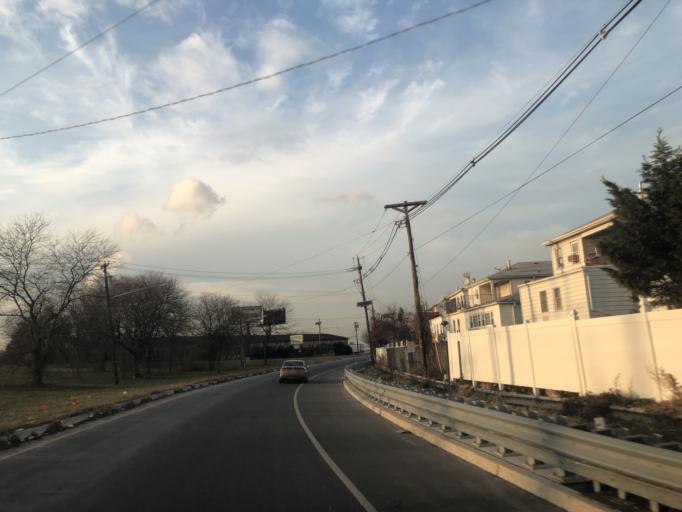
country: US
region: New Jersey
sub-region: Hudson County
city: Bayonne
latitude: 40.6952
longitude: -74.1048
